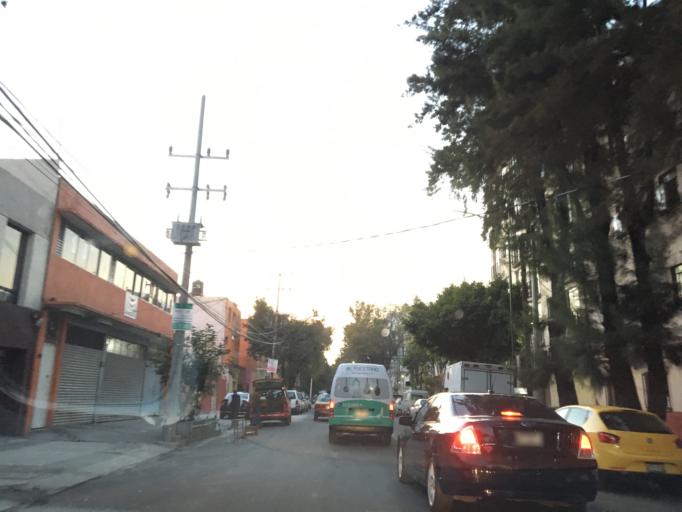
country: MX
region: Mexico City
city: Benito Juarez
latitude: 19.4173
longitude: -99.1483
